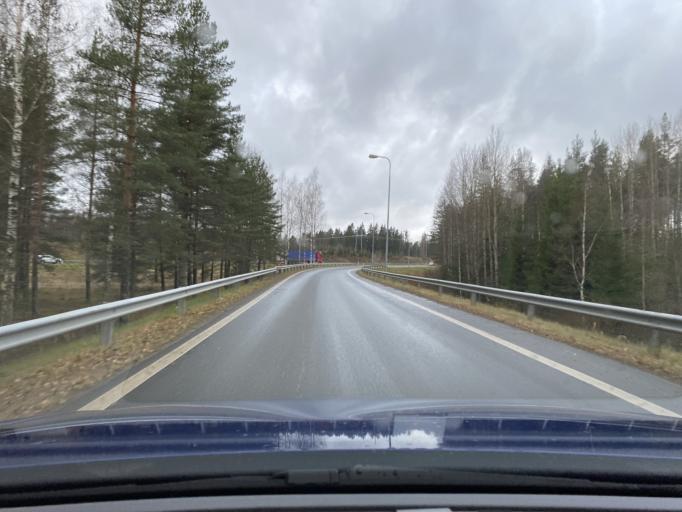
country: FI
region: Pirkanmaa
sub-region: Tampere
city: Lempaeaelae
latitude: 61.3992
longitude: 23.7825
